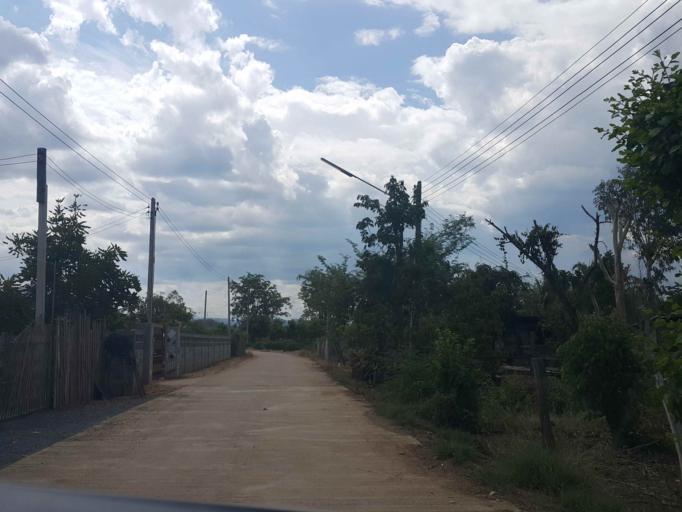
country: TH
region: Sukhothai
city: Thung Saliam
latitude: 17.3276
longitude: 99.4403
